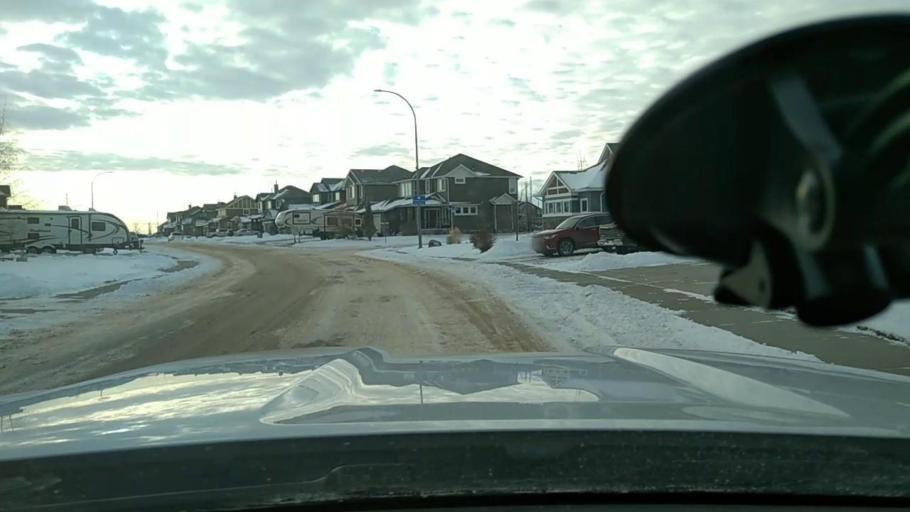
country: CA
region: Alberta
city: Chestermere
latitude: 50.9630
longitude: -113.6628
